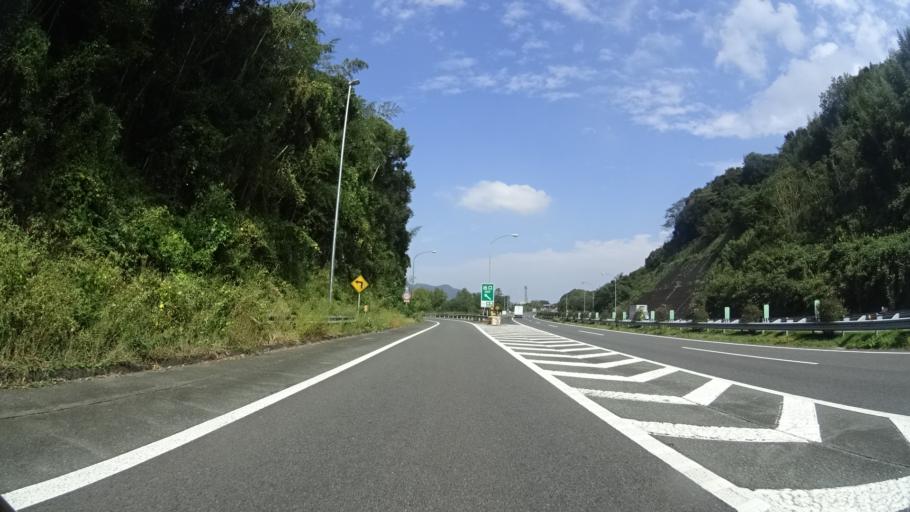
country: JP
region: Kumamoto
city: Matsubase
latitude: 32.6457
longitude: 130.7069
